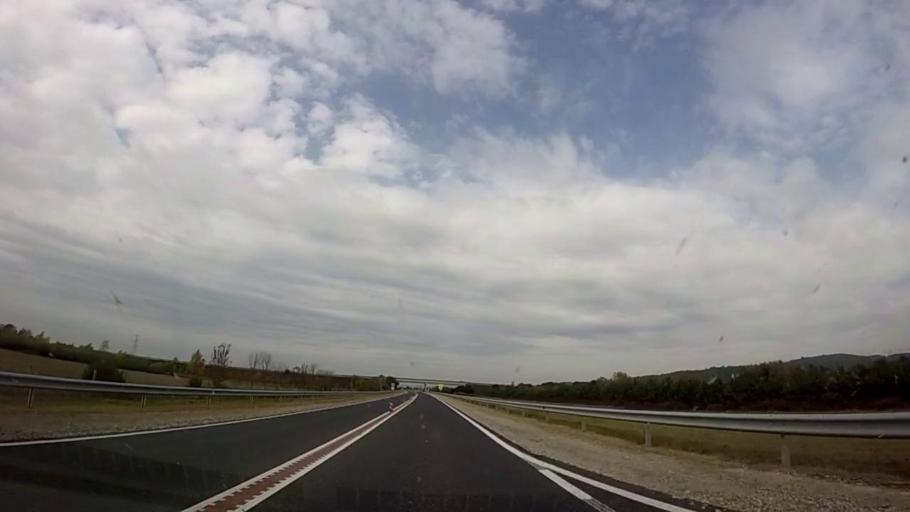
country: HR
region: Medimurska
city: Domasinec
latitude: 46.4994
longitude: 16.6197
